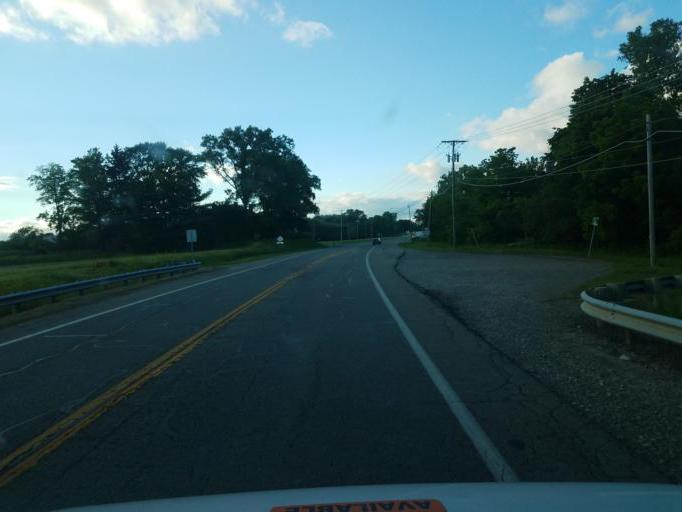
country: US
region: Ohio
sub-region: Knox County
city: Mount Vernon
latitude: 40.3915
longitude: -82.5074
